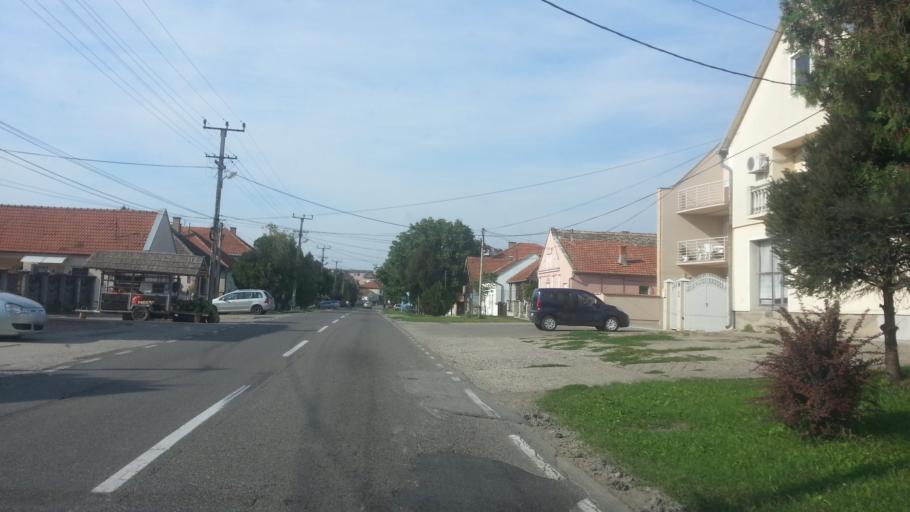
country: RS
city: Novi Banovci
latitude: 44.9532
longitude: 20.2815
